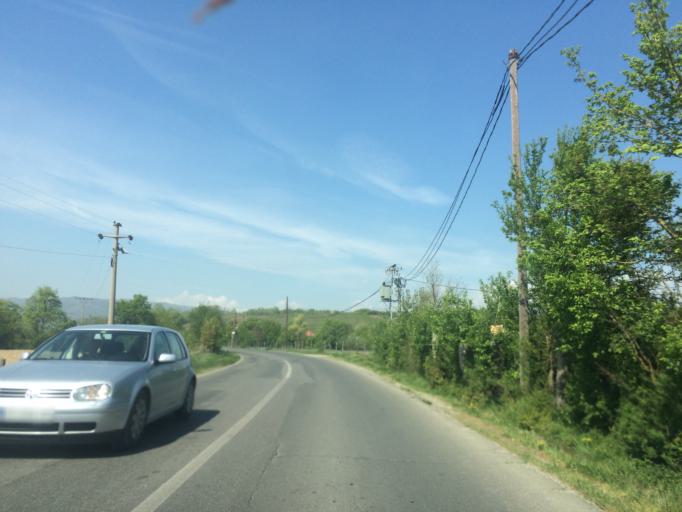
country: XK
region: Gjakova
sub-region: Komuna e Gjakoves
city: Gjakove
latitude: 42.3766
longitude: 20.3839
